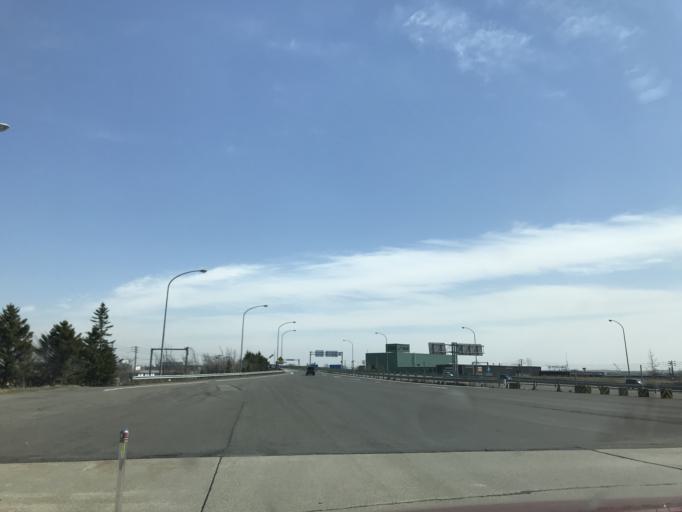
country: JP
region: Hokkaido
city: Sapporo
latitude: 43.0799
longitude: 141.4270
